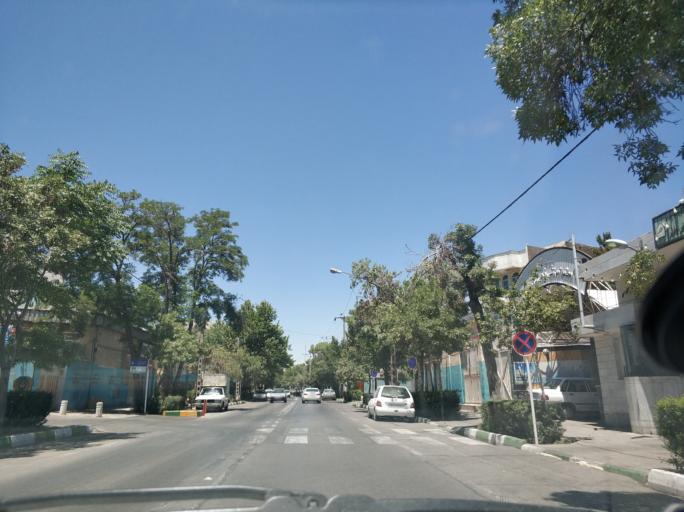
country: IR
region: Razavi Khorasan
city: Mashhad
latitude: 36.2763
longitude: 59.5905
